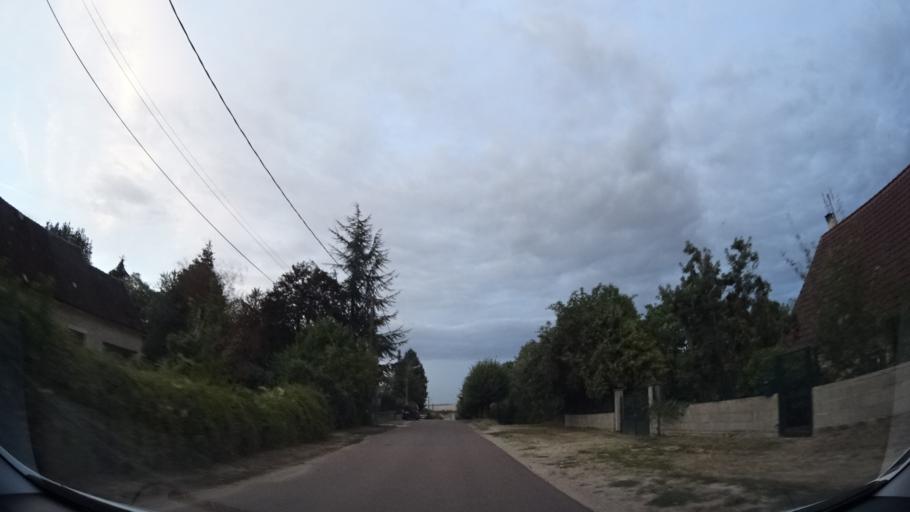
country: FR
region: Bourgogne
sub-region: Departement de l'Yonne
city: Aillant-sur-Tholon
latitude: 47.9174
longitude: 3.3284
